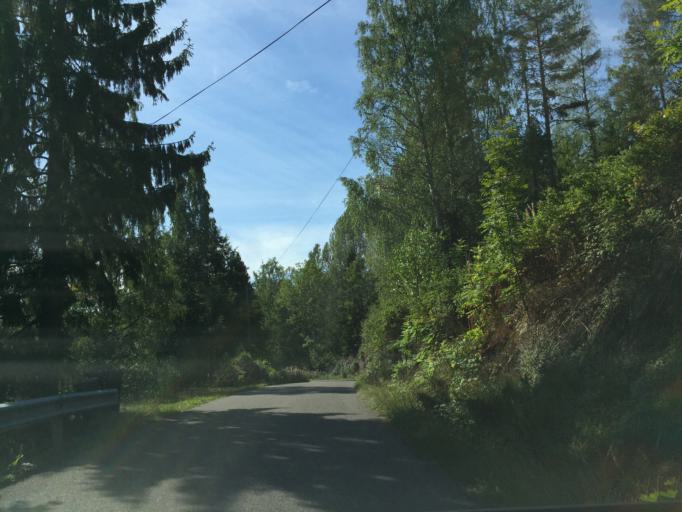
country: NO
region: Vestfold
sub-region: Hof
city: Hof
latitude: 59.4733
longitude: 10.1432
